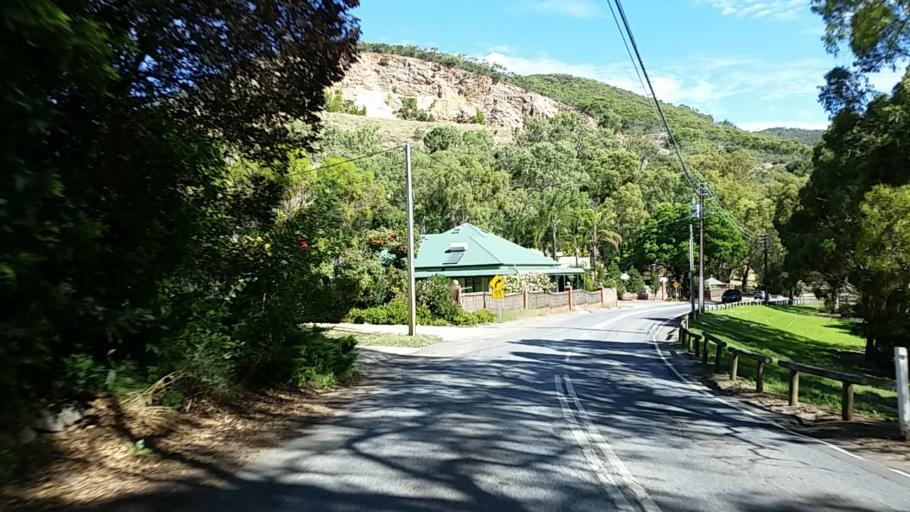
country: AU
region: South Australia
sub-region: Campbelltown
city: Athelstone
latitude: -34.8613
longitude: 138.7212
